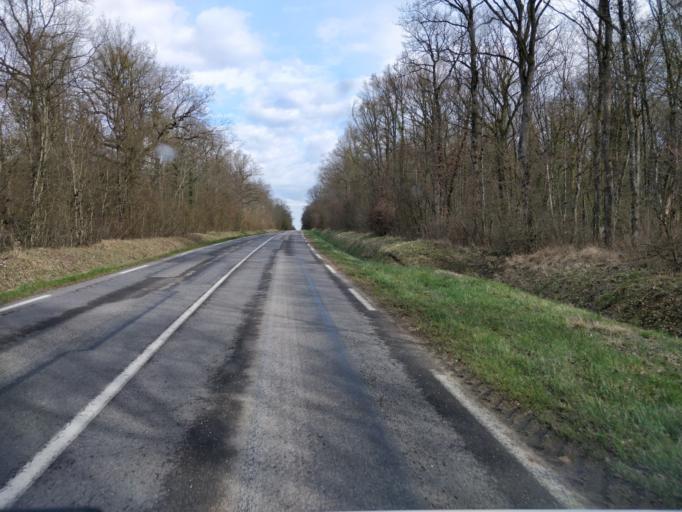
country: FR
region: Lorraine
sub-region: Departement de Meurthe-et-Moselle
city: Doncourt-les-Conflans
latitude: 49.0596
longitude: 5.8911
